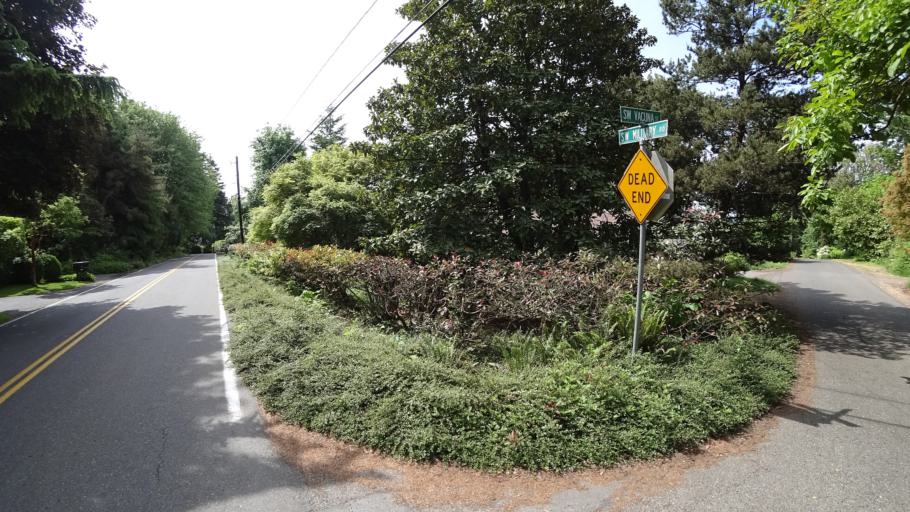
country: US
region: Oregon
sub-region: Clackamas County
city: Lake Oswego
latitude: 45.4420
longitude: -122.6672
